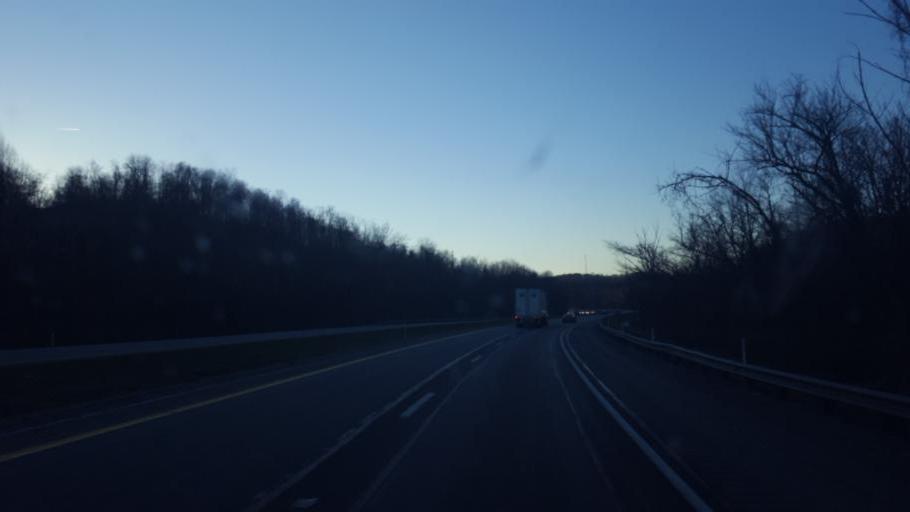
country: US
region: West Virginia
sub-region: Brooke County
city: Bethany
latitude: 40.1145
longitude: -80.4664
